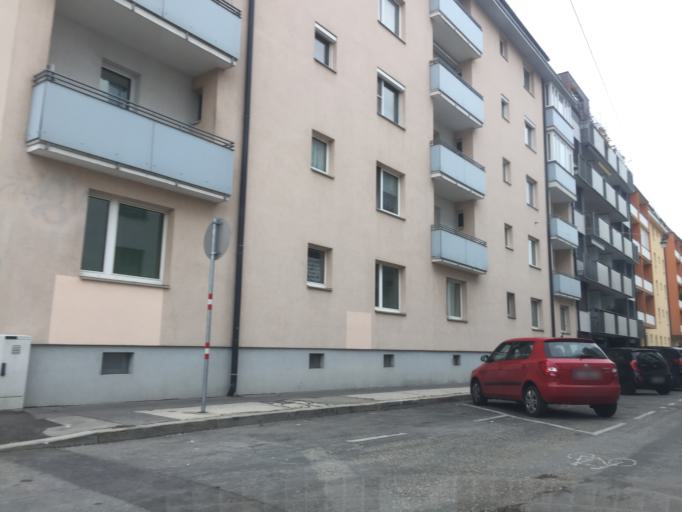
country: AT
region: Vienna
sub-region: Wien Stadt
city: Vienna
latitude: 48.1963
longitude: 16.2918
